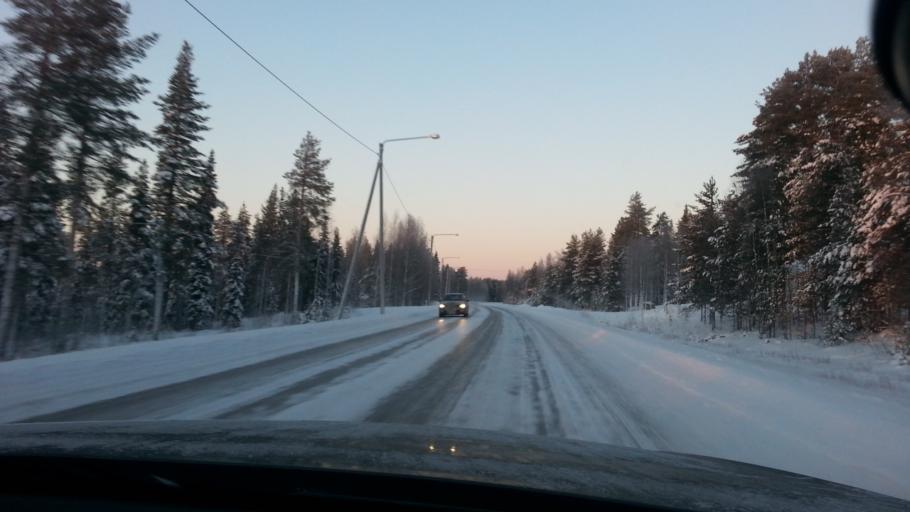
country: FI
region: Lapland
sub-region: Tunturi-Lappi
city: Kittilae
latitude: 67.0401
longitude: 25.1002
